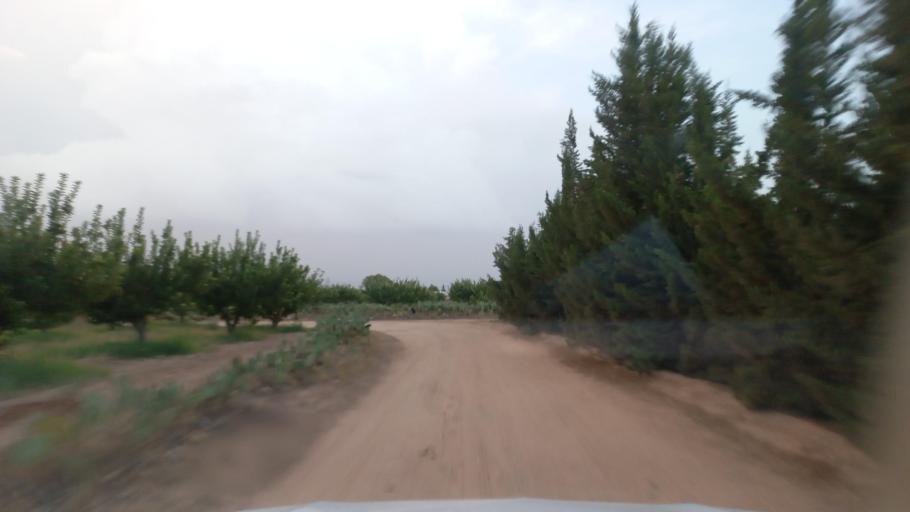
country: TN
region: Al Qasrayn
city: Kasserine
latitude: 35.2770
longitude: 9.0352
